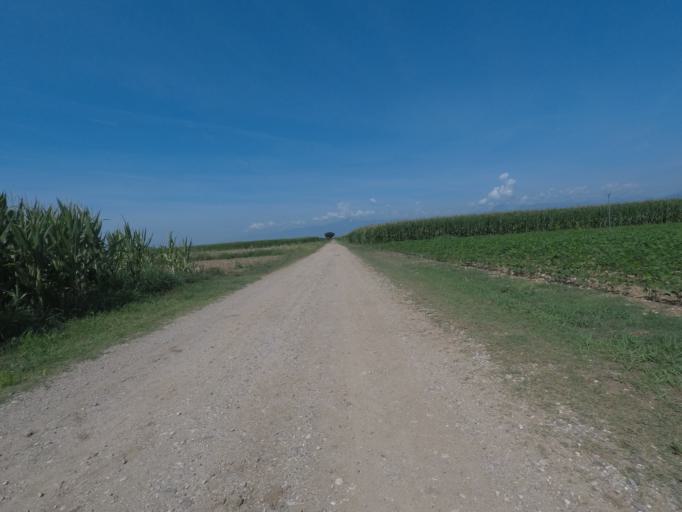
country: IT
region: Friuli Venezia Giulia
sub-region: Provincia di Udine
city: Flaibano
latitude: 46.0822
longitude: 12.9729
